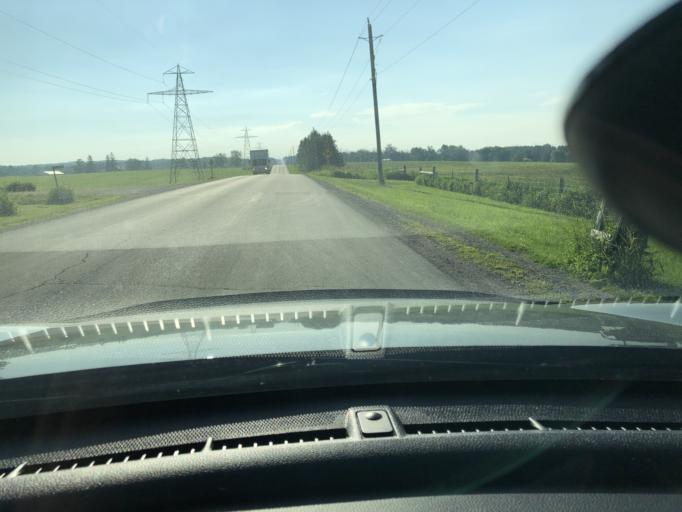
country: CA
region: Ontario
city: Stratford
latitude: 43.3884
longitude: -80.8848
